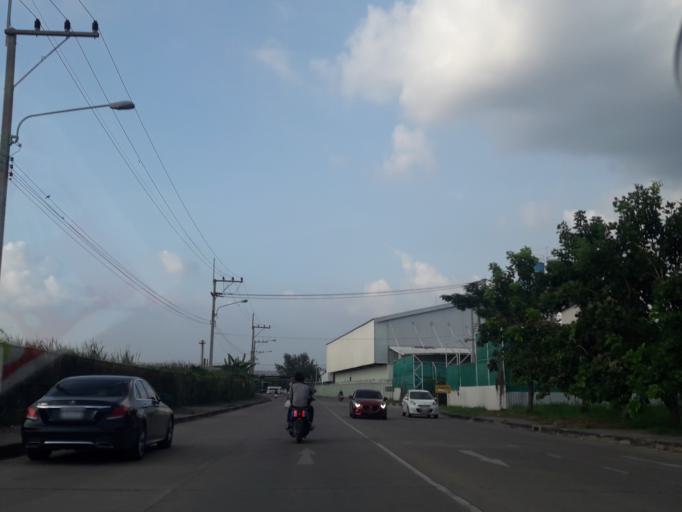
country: TH
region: Phra Nakhon Si Ayutthaya
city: Ban Bang Kadi Pathum Thani
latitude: 13.9962
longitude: 100.6179
